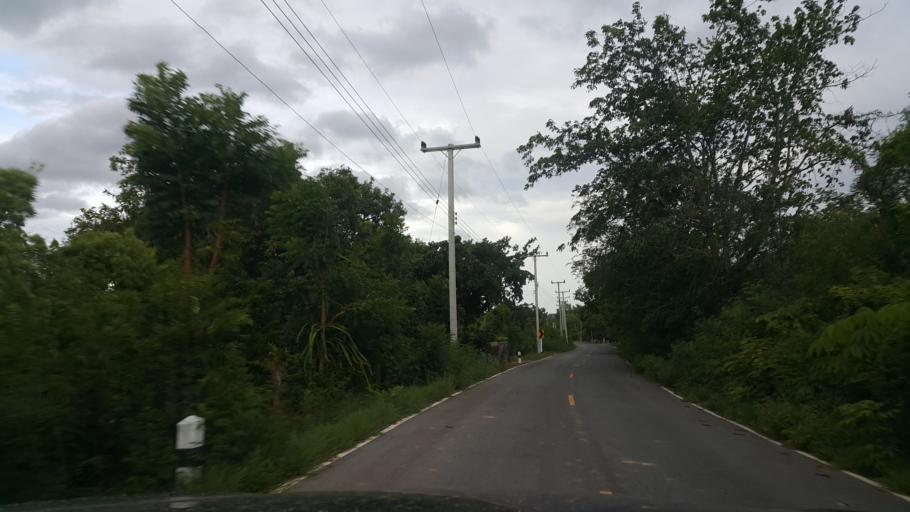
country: TH
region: Sukhothai
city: Ban Dan Lan Hoi
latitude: 17.1592
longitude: 99.5058
